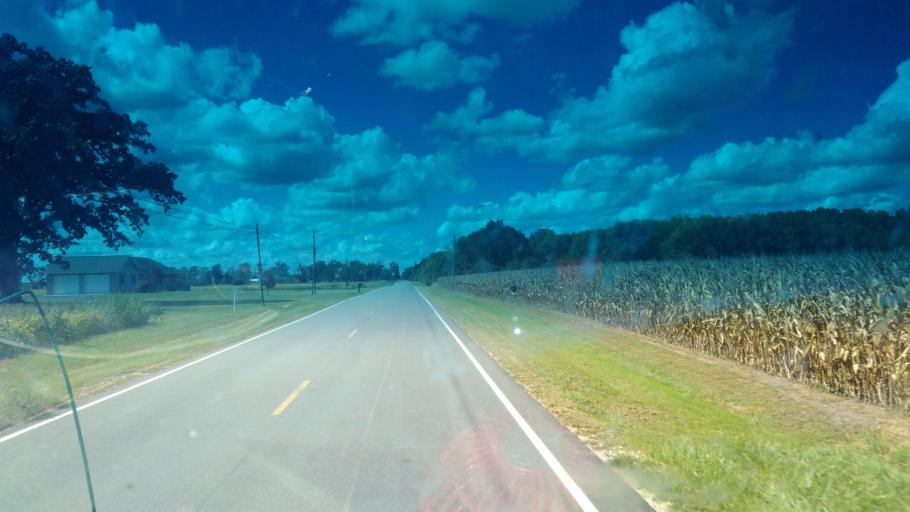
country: US
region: Ohio
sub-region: Champaign County
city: North Lewisburg
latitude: 40.1896
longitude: -83.4648
